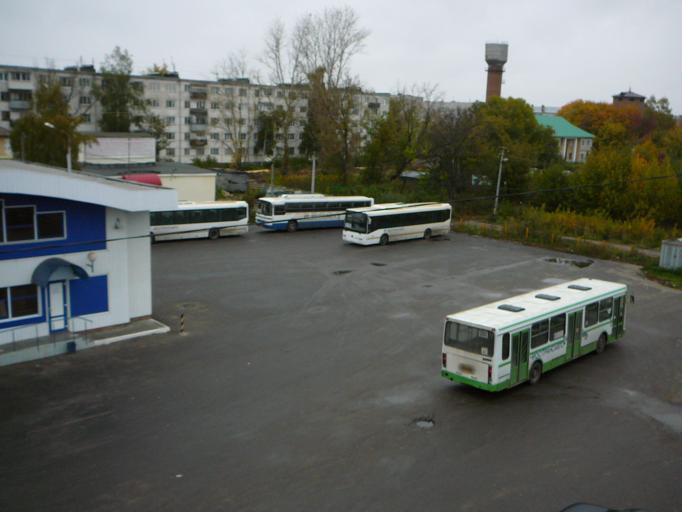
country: RU
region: Moskovskaya
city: Kurovskoye
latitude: 55.5733
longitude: 38.9241
